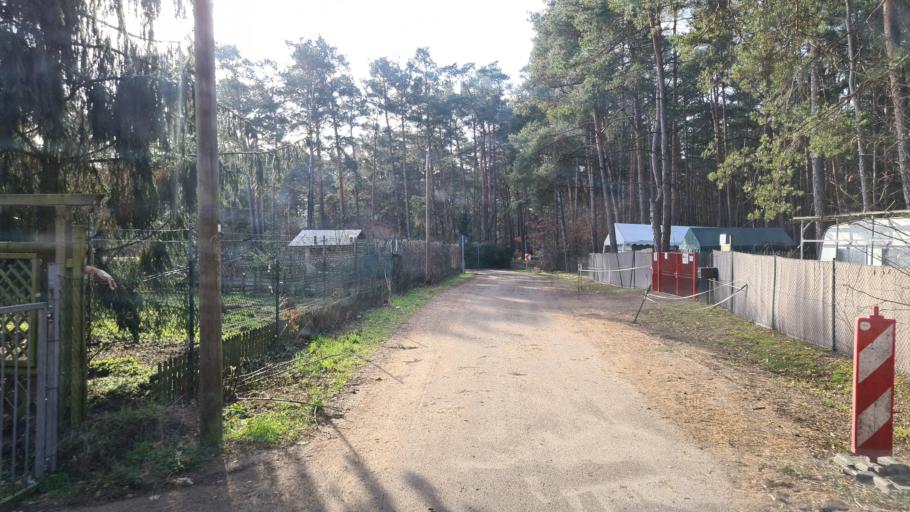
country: DE
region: Brandenburg
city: Gross Koris
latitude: 52.1602
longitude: 13.6898
